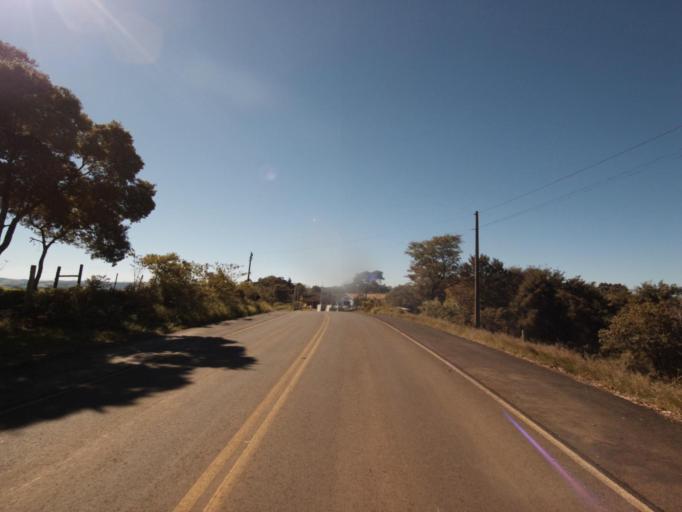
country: AR
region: Misiones
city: Bernardo de Irigoyen
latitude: -26.7088
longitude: -53.5261
